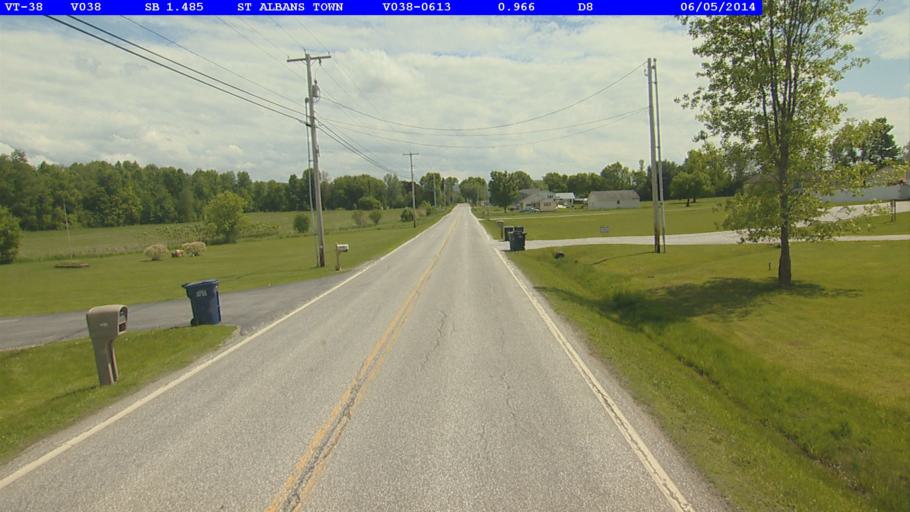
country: US
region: Vermont
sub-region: Franklin County
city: Saint Albans
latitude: 44.8361
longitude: -73.0986
